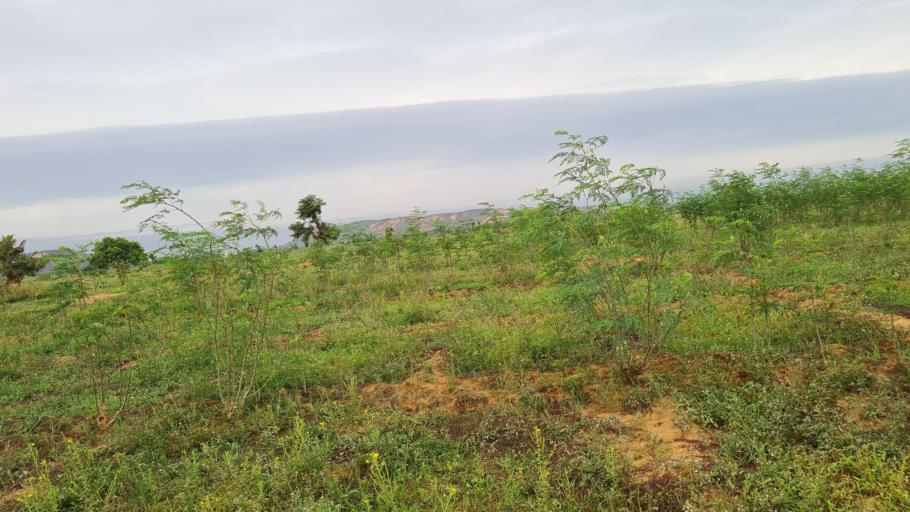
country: NE
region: Tahoua
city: Birni N Konni
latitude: 13.8365
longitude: 5.2680
